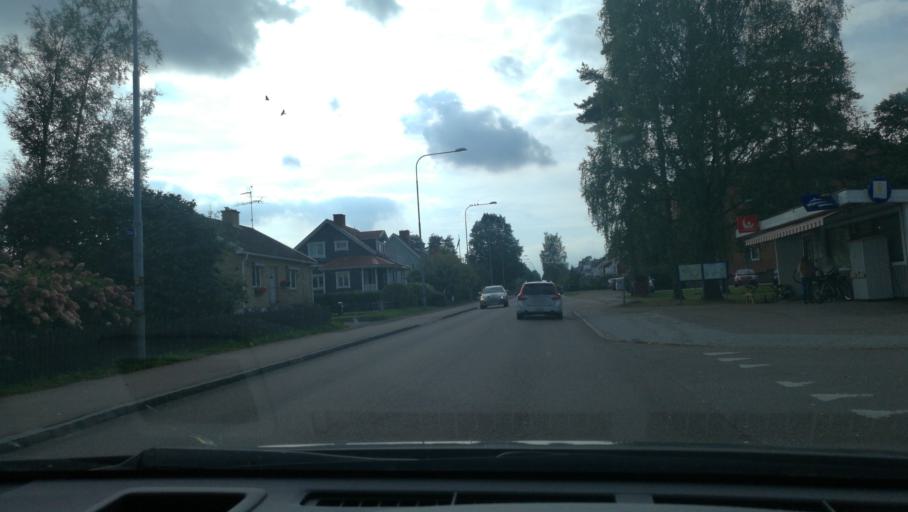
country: SE
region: Dalarna
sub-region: Avesta Kommun
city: Avesta
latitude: 60.1614
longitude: 16.1873
